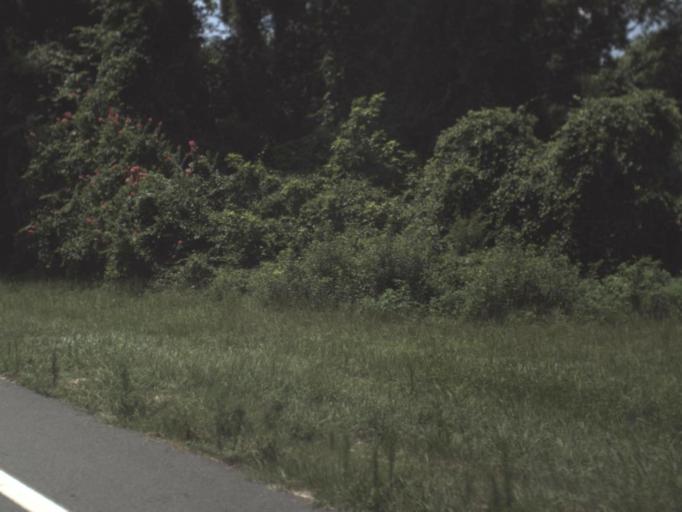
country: US
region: Florida
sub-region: Suwannee County
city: Wellborn
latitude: 30.3498
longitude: -82.7728
